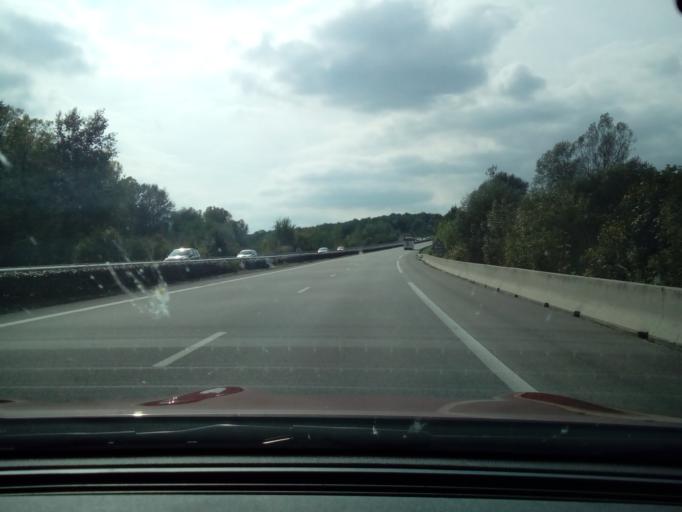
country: FR
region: Rhone-Alpes
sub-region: Departement de l'Isere
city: Vinay
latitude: 45.2120
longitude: 5.4697
